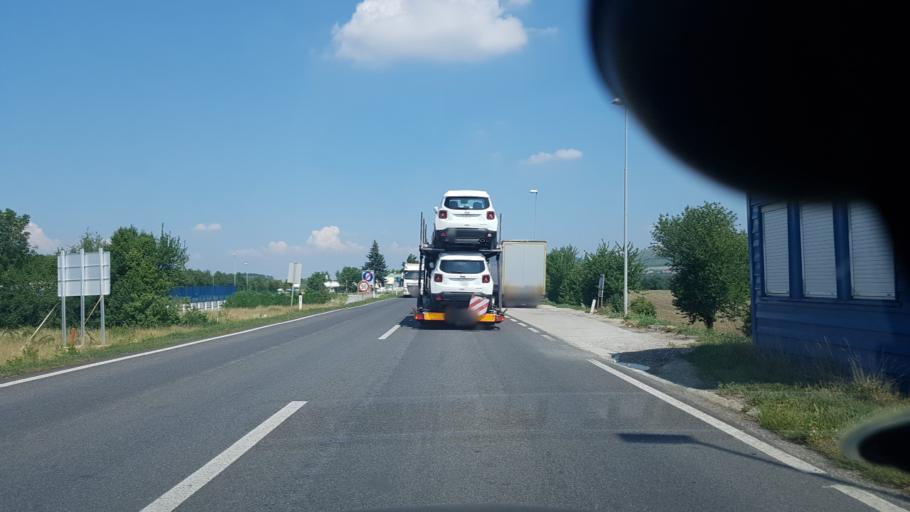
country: AT
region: Lower Austria
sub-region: Politischer Bezirk Mistelbach
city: Drasenhofen
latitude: 48.7755
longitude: 16.6416
